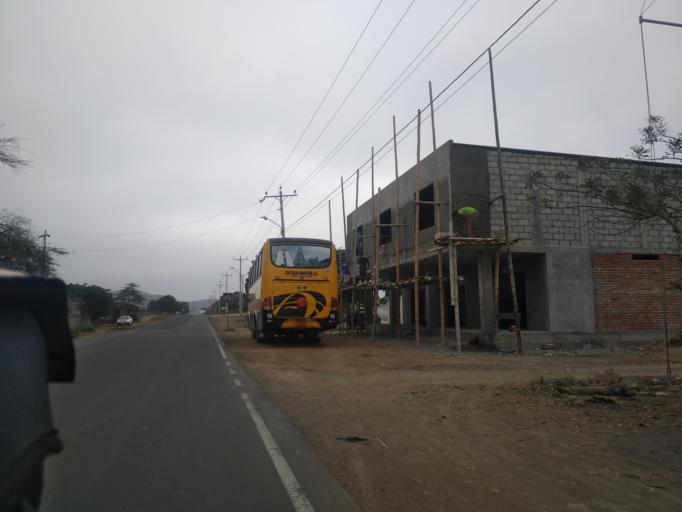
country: EC
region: Manabi
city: Montecristi
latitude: -1.0809
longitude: -80.6749
